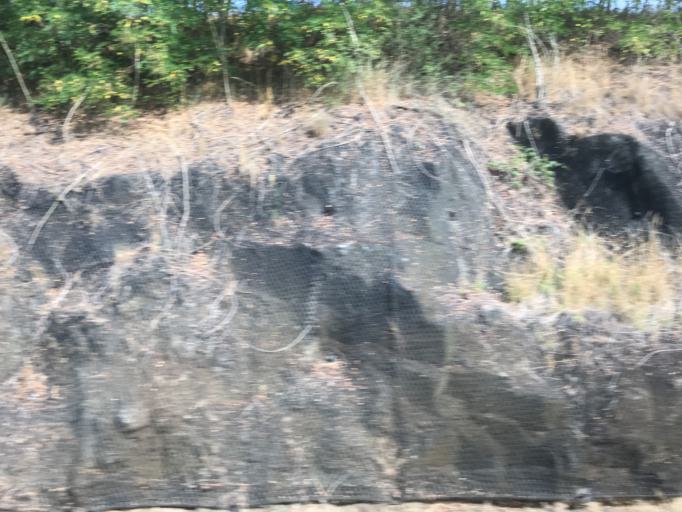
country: CZ
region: Central Bohemia
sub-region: Okres Benesov
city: Cercany
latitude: 49.8633
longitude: 14.7041
